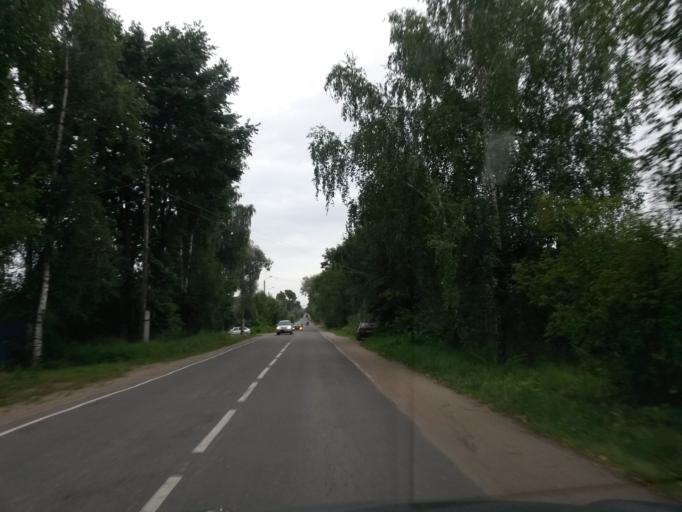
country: RU
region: Jaroslavl
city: Tutayev
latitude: 57.8851
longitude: 39.5446
